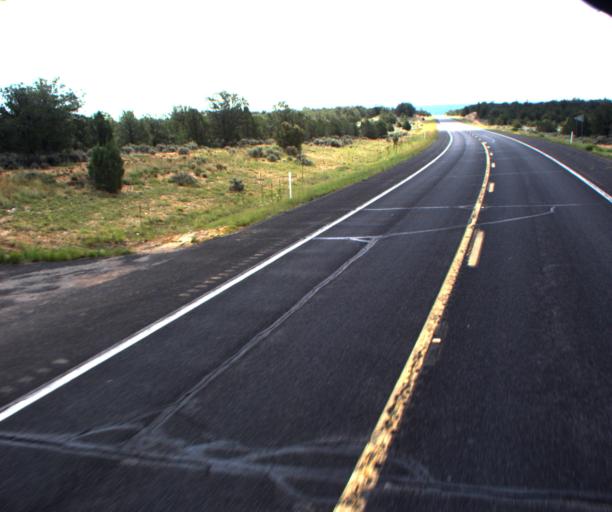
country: US
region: Arizona
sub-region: Coconino County
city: Grand Canyon
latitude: 35.9872
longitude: -111.7986
